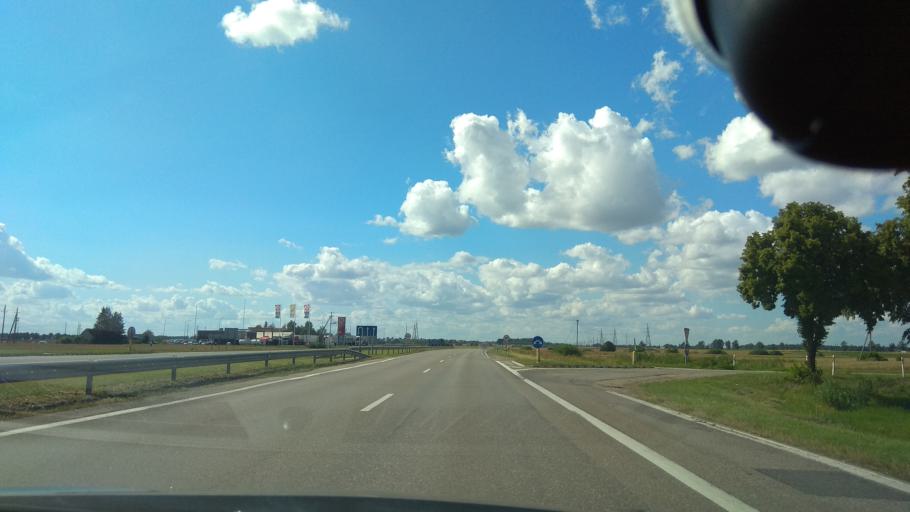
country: LT
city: Kursenai
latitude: 55.9989
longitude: 22.9936
